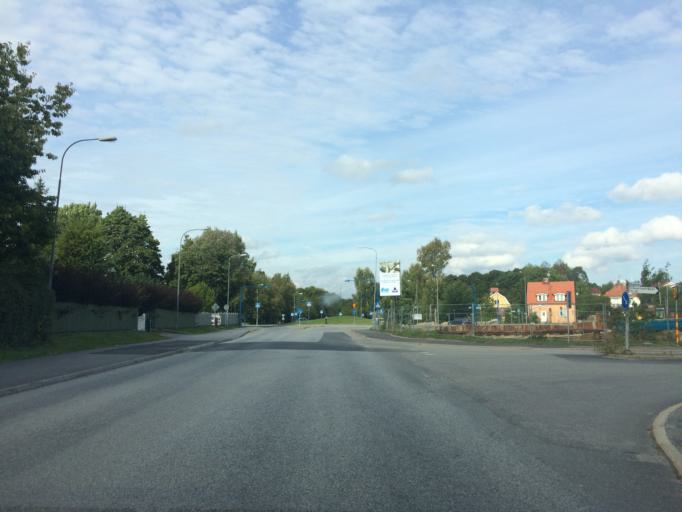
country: SE
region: Stockholm
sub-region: Sollentuna Kommun
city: Sollentuna
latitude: 59.4287
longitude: 17.9358
